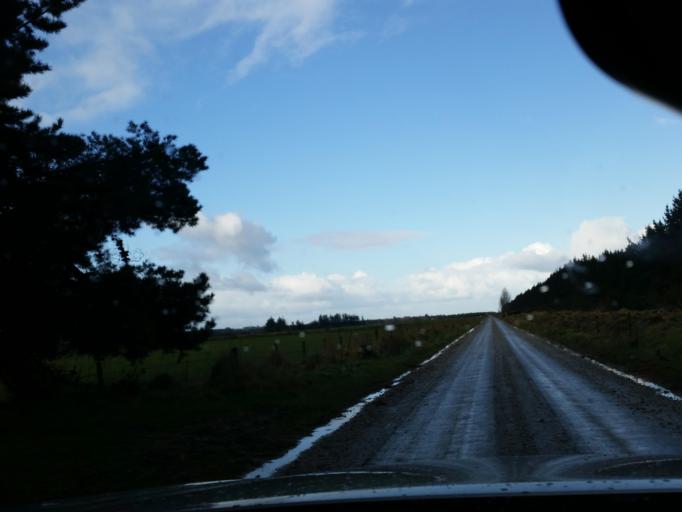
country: NZ
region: Southland
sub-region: Southland District
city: Winton
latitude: -46.2223
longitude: 168.4928
